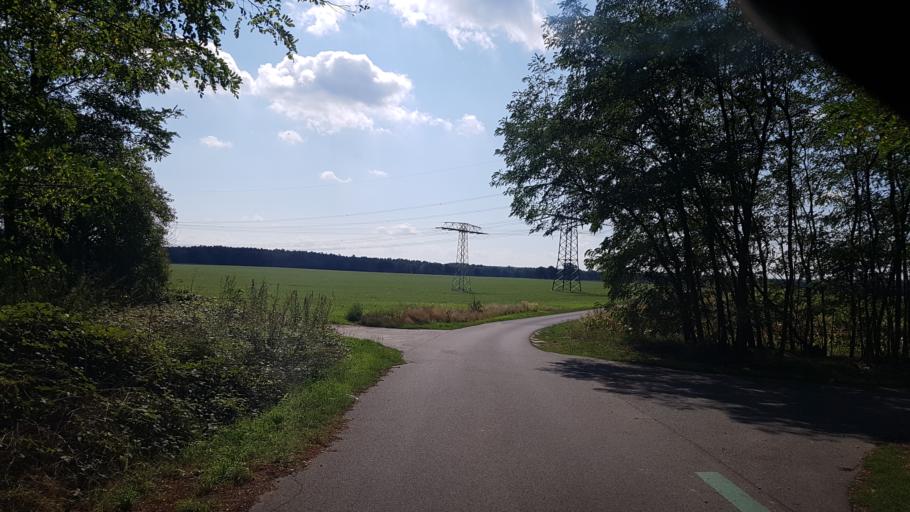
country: DE
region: Brandenburg
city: Drebkau
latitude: 51.6608
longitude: 14.2460
